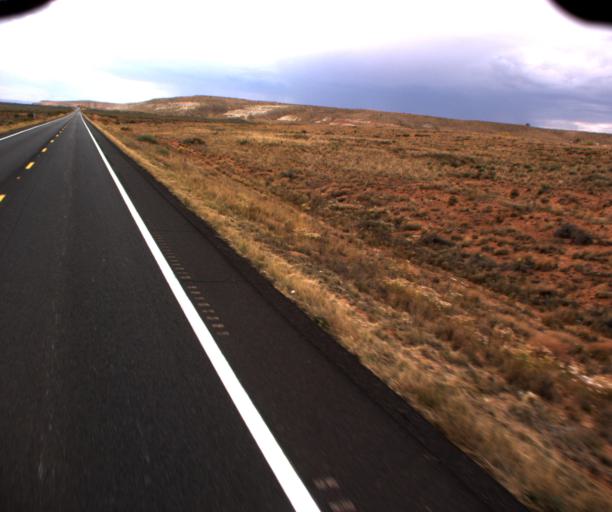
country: US
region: Arizona
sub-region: Coconino County
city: Kaibito
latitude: 36.3462
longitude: -110.9134
